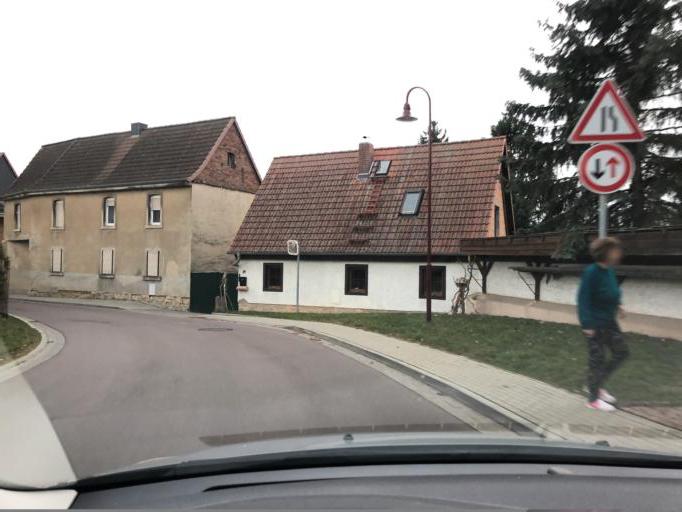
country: DE
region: Saxony-Anhalt
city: Bad Bibra
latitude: 51.1772
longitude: 11.5989
